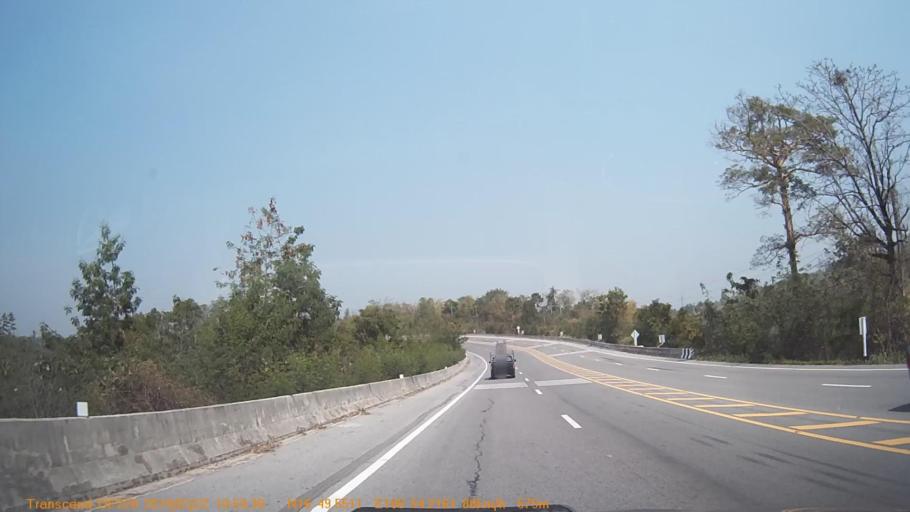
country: TH
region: Phetchabun
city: Khao Kho
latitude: 16.8263
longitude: 100.9032
